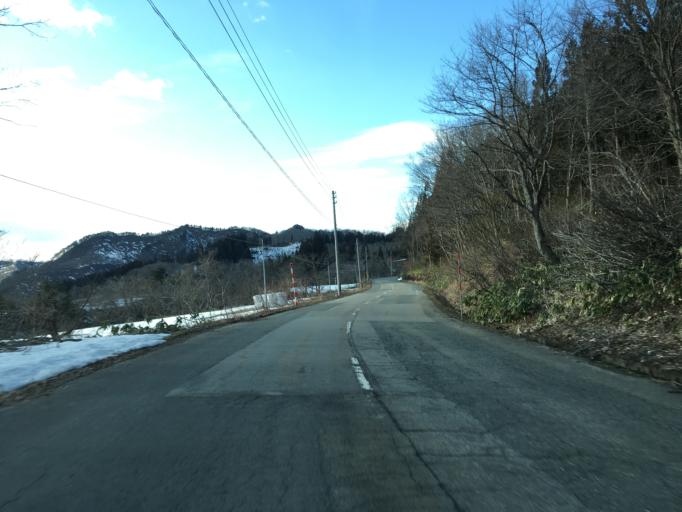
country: JP
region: Yamagata
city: Yonezawa
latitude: 37.9243
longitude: 139.9195
